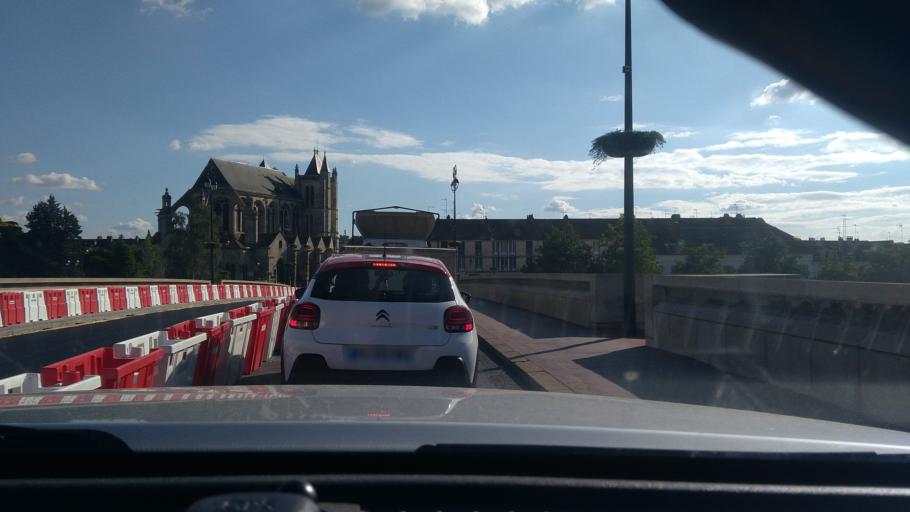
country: FR
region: Ile-de-France
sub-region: Departement de Seine-et-Marne
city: Montereau-Fault-Yonne
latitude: 48.3879
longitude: 2.9594
